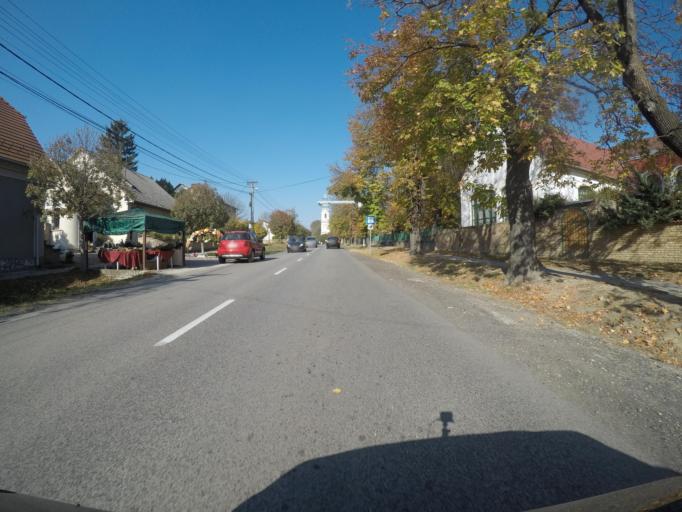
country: HU
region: Tolna
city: Nagydorog
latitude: 46.6273
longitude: 18.6564
